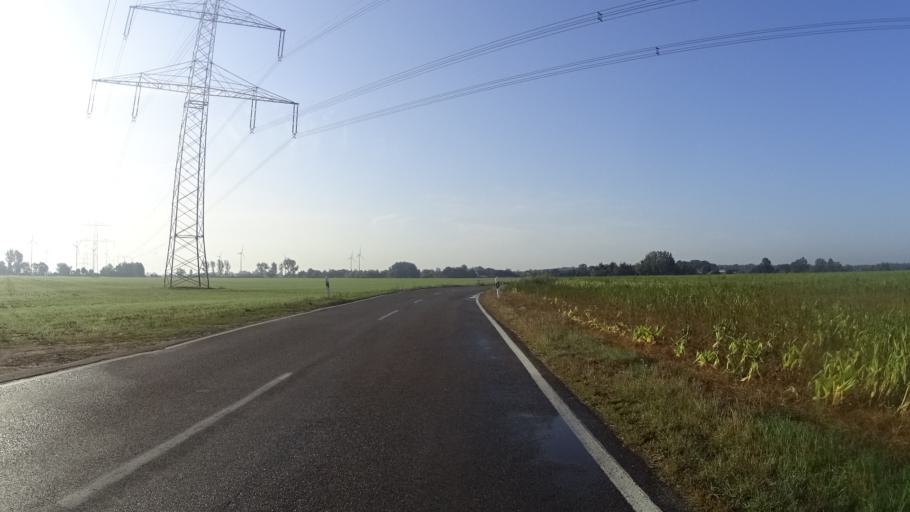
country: DE
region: Brandenburg
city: Kasel-Golzig
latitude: 51.9967
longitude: 13.6910
